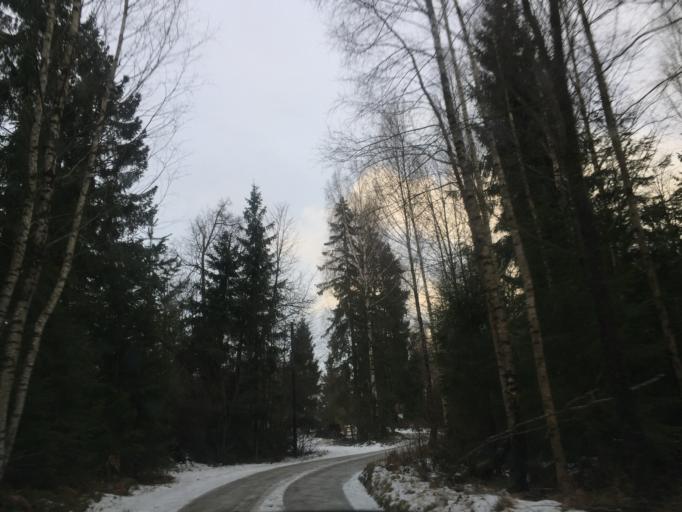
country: NO
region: Ostfold
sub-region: Moss
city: Moss
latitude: 59.4897
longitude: 10.6662
